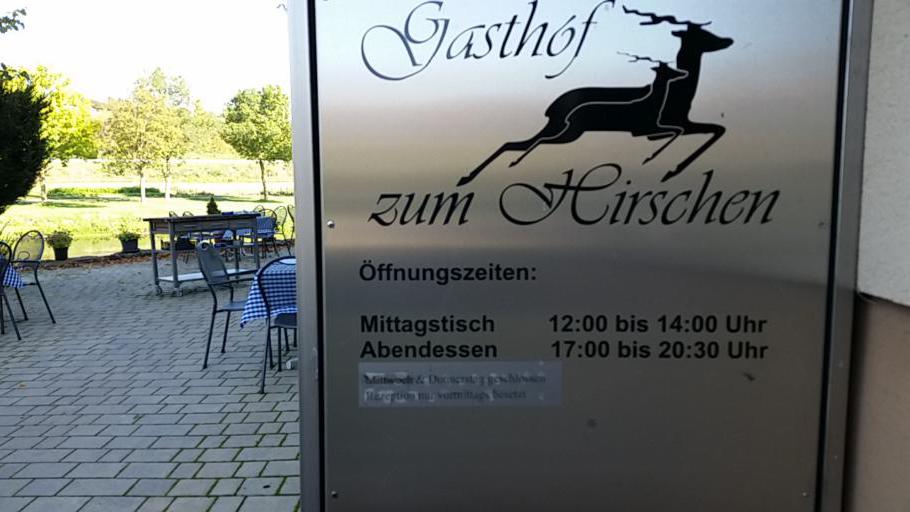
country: DE
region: Bavaria
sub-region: Regierungsbezirk Unterfranken
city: Tauberrettersheim
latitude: 49.4957
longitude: 9.9357
